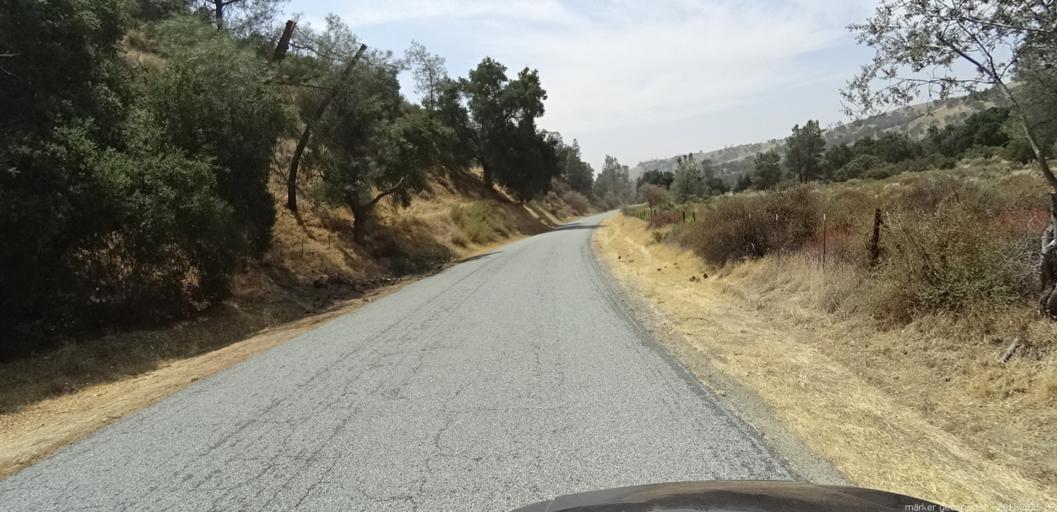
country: US
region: California
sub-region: San Luis Obispo County
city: San Miguel
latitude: 35.8859
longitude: -120.5594
